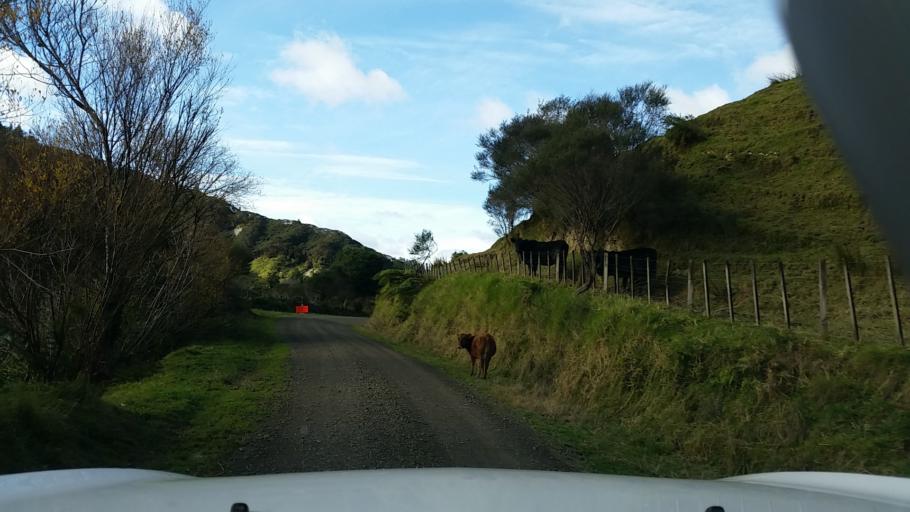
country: NZ
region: Taranaki
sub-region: New Plymouth District
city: Waitara
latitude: -38.9824
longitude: 174.4786
